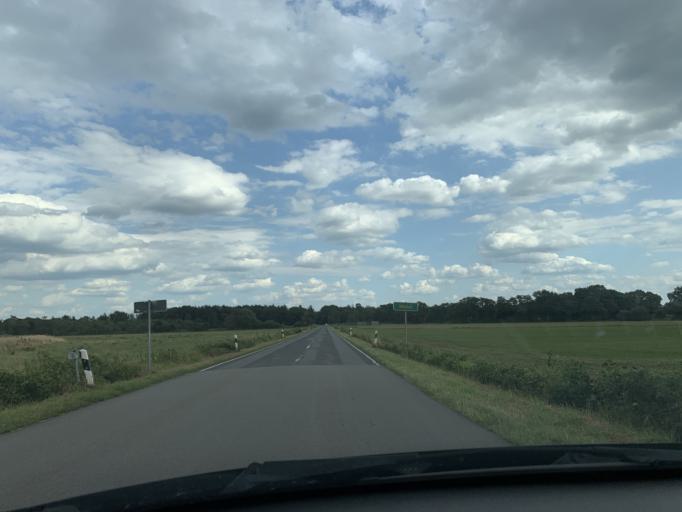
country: DE
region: Lower Saxony
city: Apen
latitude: 53.2249
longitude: 7.8330
